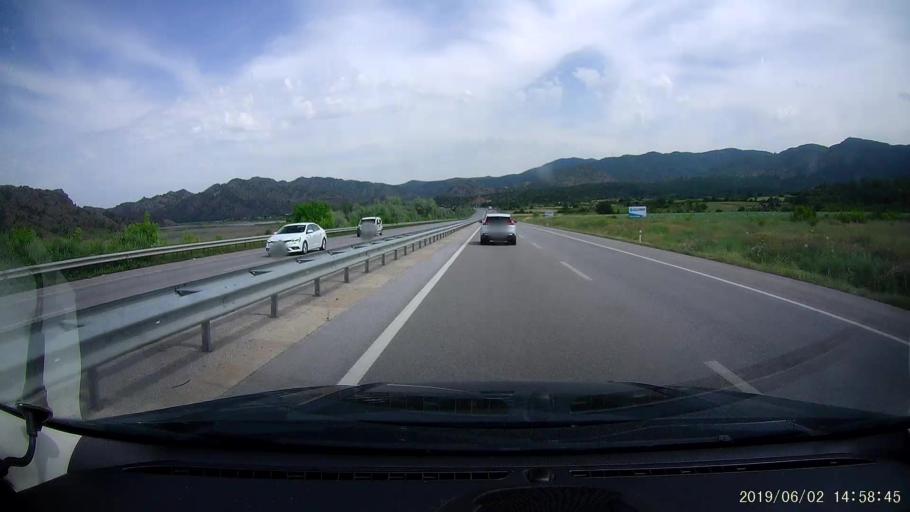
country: TR
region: Corum
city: Osmancik
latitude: 40.9777
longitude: 34.6829
